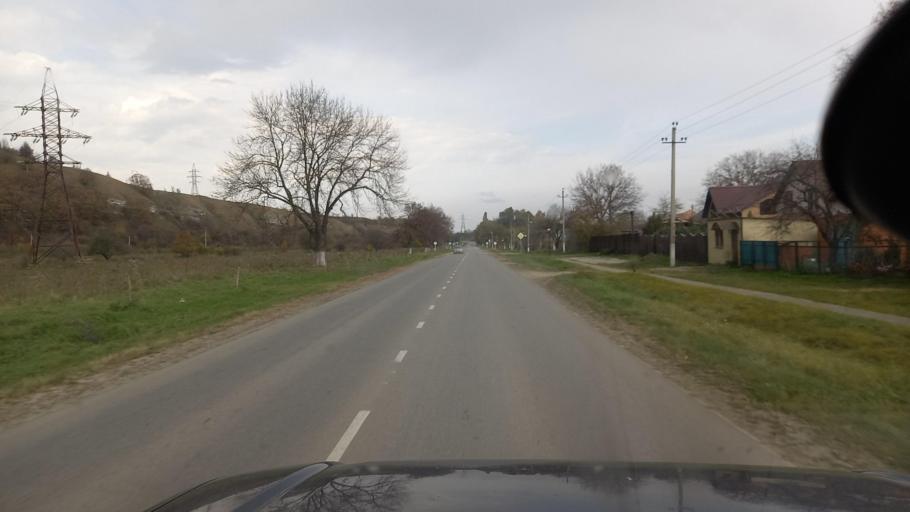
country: RU
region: Krasnodarskiy
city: Psebay
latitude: 44.1581
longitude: 40.8354
